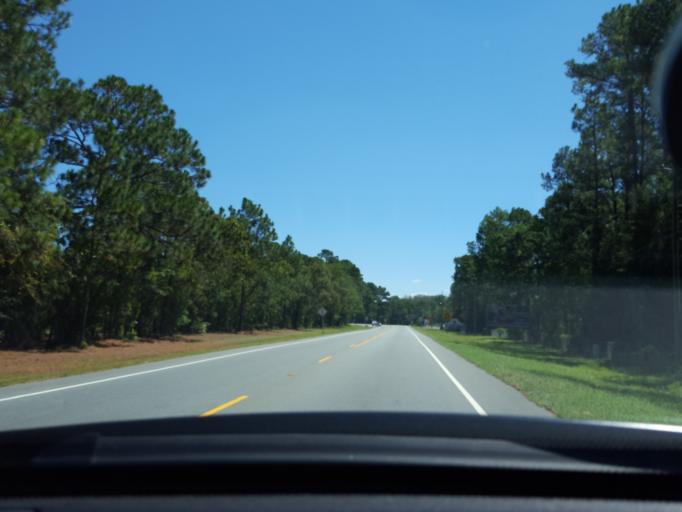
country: US
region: North Carolina
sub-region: Bladen County
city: Elizabethtown
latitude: 34.6489
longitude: -78.5316
